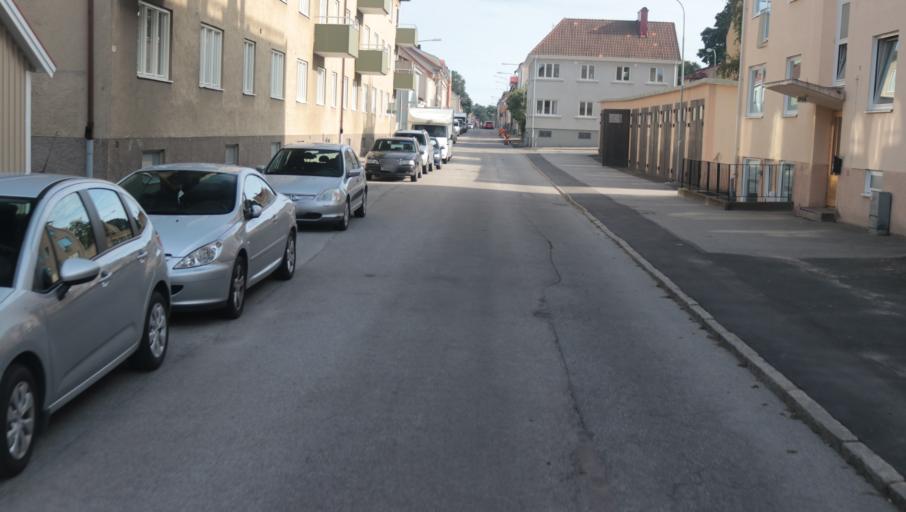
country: SE
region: Blekinge
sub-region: Karlshamns Kommun
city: Karlshamn
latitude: 56.1741
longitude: 14.8650
